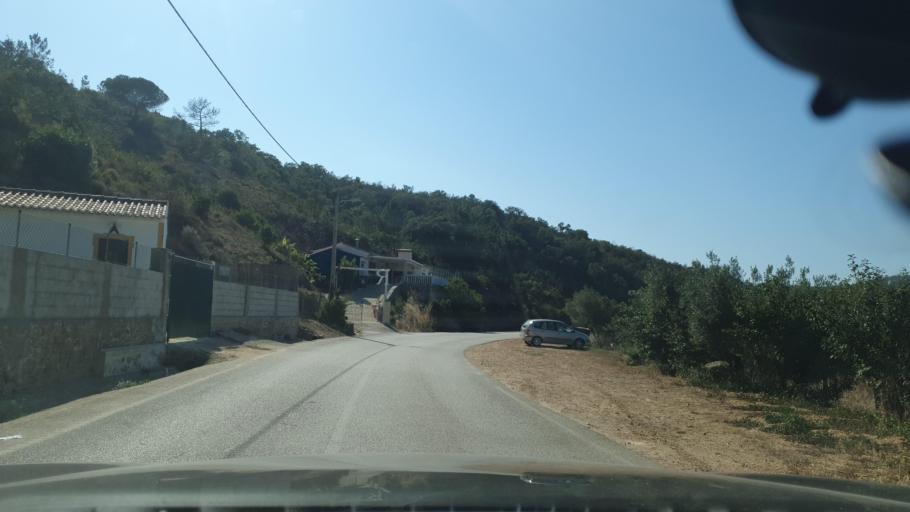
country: PT
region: Beja
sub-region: Odemira
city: Sao Teotonio
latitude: 37.4327
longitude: -8.7834
